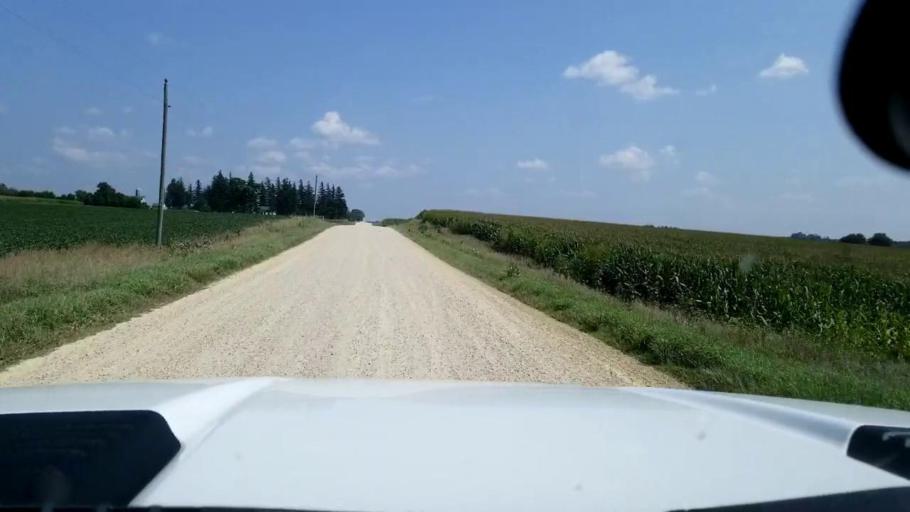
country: US
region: Minnesota
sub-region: Goodhue County
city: Wanamingo
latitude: 44.3416
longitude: -92.8911
